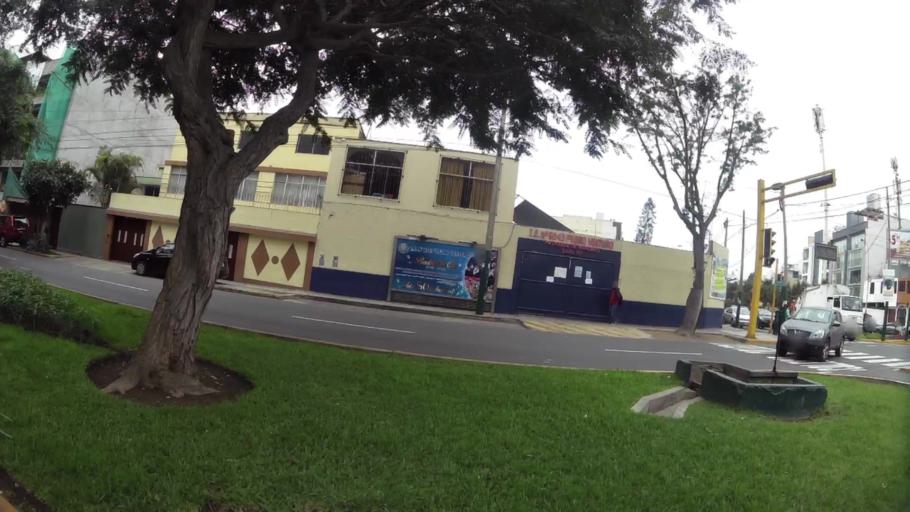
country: PE
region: Lima
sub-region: Lima
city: Surco
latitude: -12.1243
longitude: -76.9904
